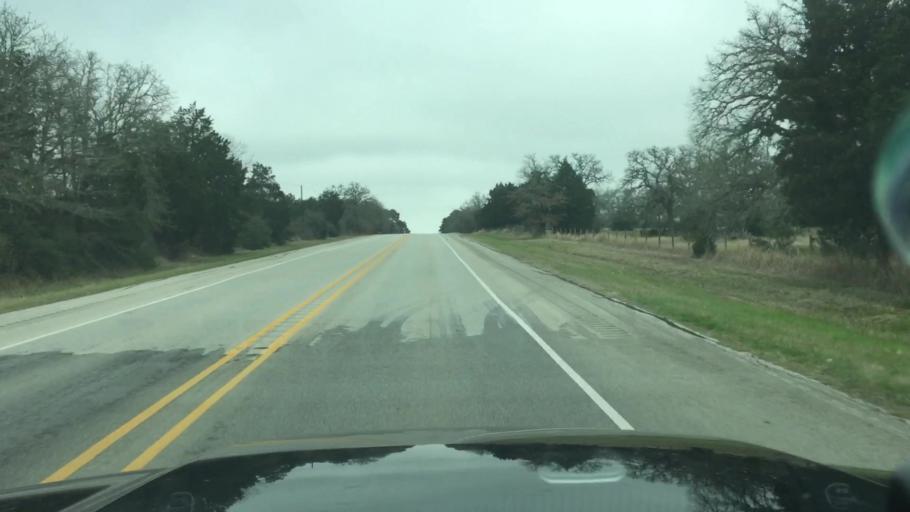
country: US
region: Texas
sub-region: Lee County
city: Giddings
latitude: 30.0751
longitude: -96.9170
